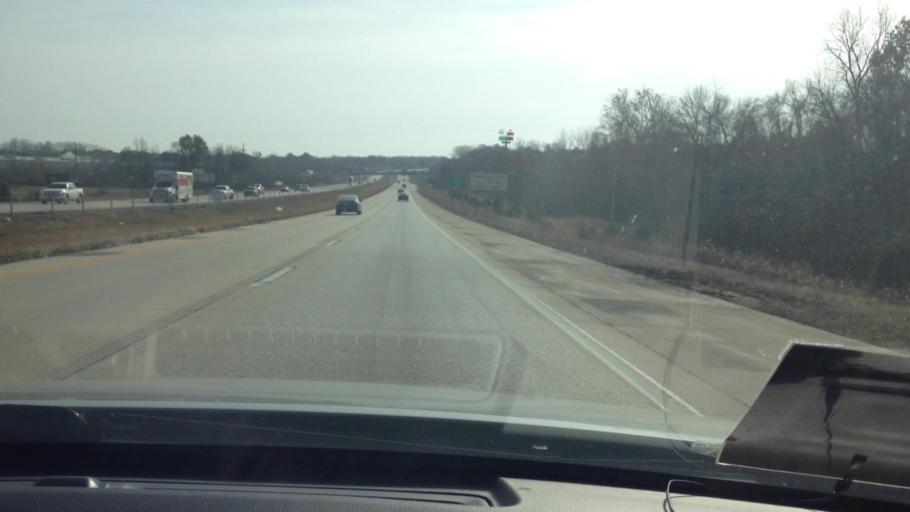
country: US
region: Missouri
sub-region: Cass County
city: Harrisonville
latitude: 38.6432
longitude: -94.3600
